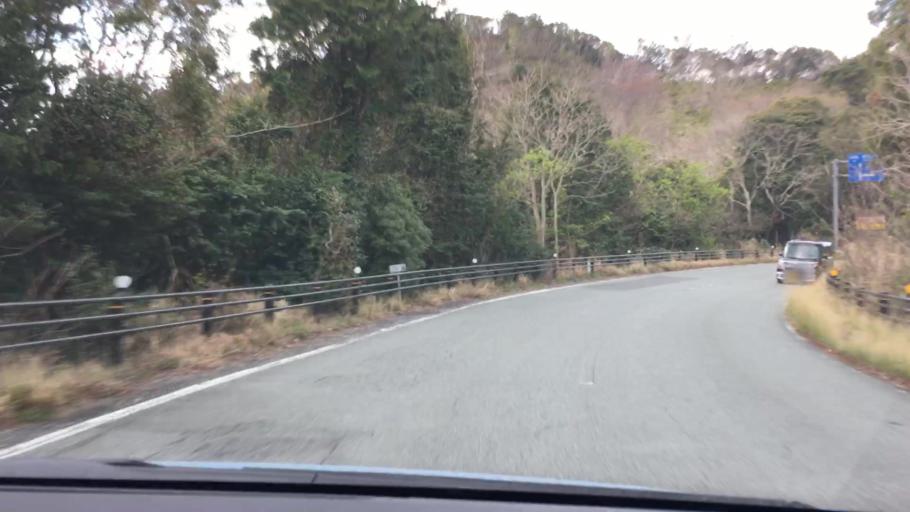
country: JP
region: Mie
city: Toba
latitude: 34.4408
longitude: 136.8934
